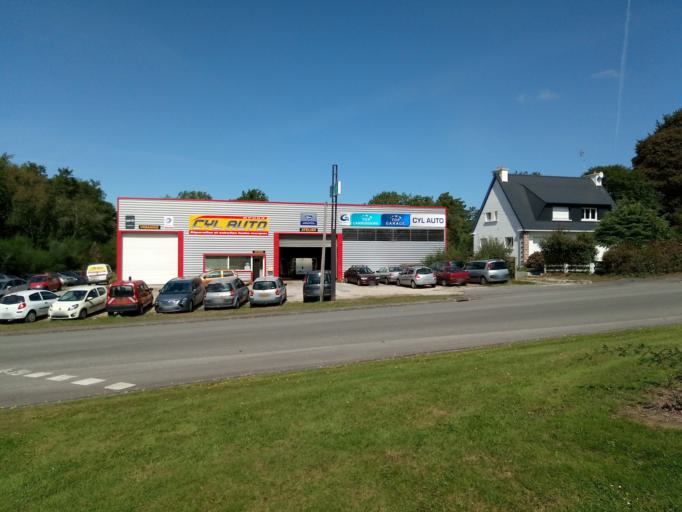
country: FR
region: Brittany
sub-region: Departement du Morbihan
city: Gourin
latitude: 48.1406
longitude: -3.6123
